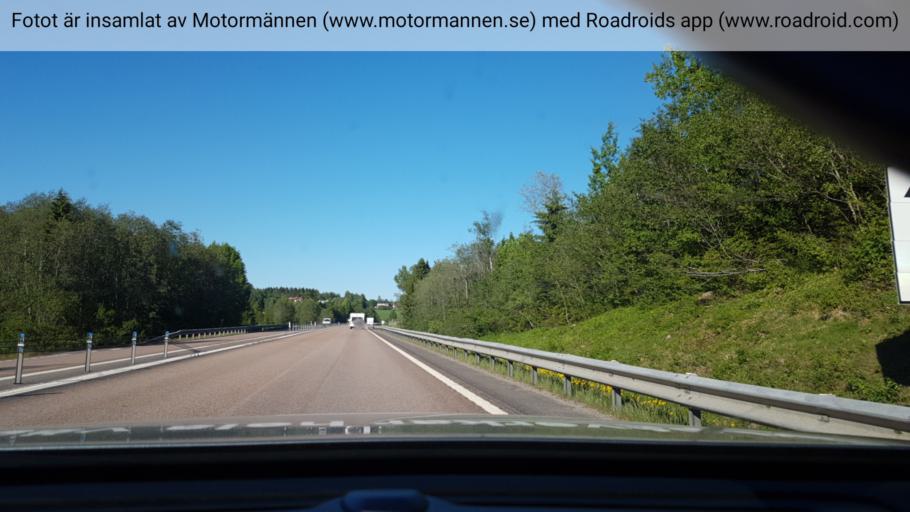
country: SE
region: Vaesternorrland
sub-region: Haernoesands Kommun
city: Haernoesand
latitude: 62.5813
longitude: 17.7653
